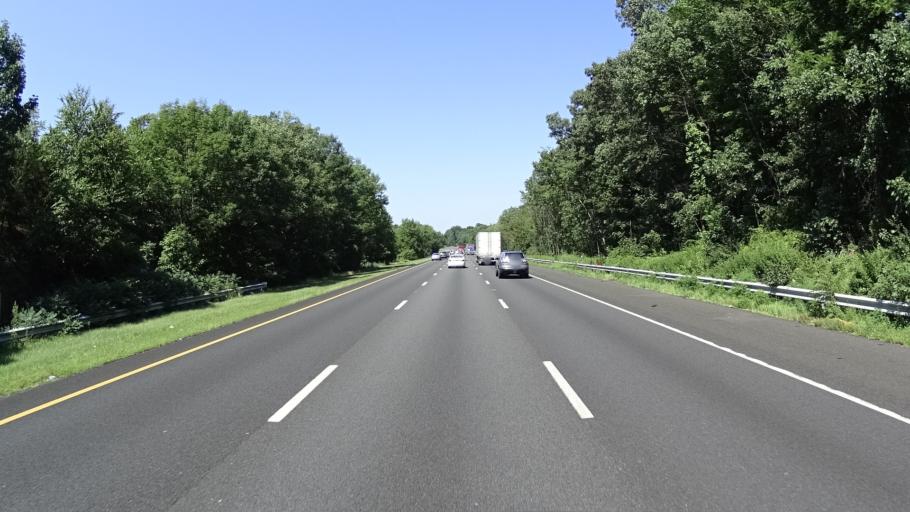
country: US
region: New Jersey
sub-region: Somerset County
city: Watchung
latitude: 40.6494
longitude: -74.4806
